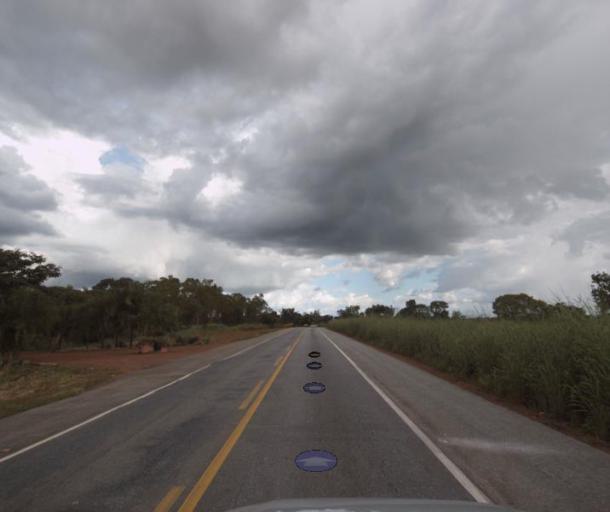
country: BR
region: Goias
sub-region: Porangatu
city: Porangatu
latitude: -13.3091
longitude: -49.1184
